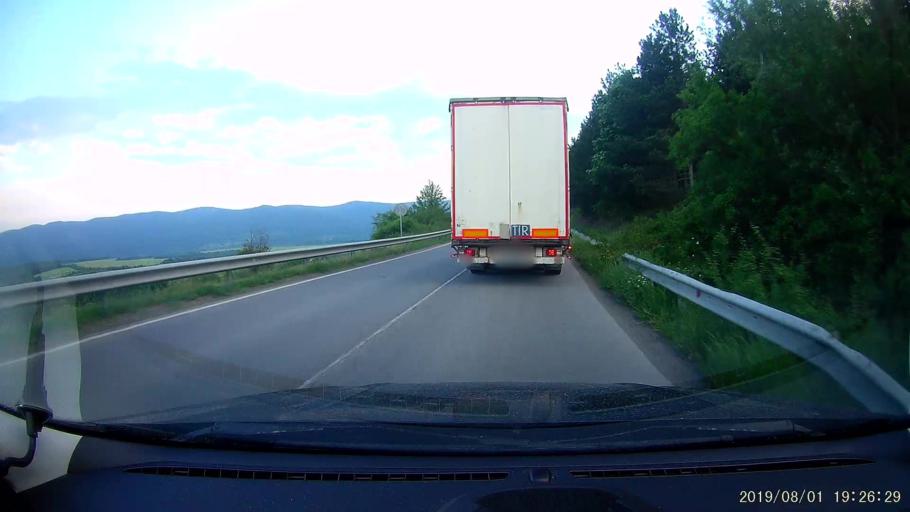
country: BG
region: Burgas
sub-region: Obshtina Sungurlare
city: Sungurlare
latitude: 42.8571
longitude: 26.9402
